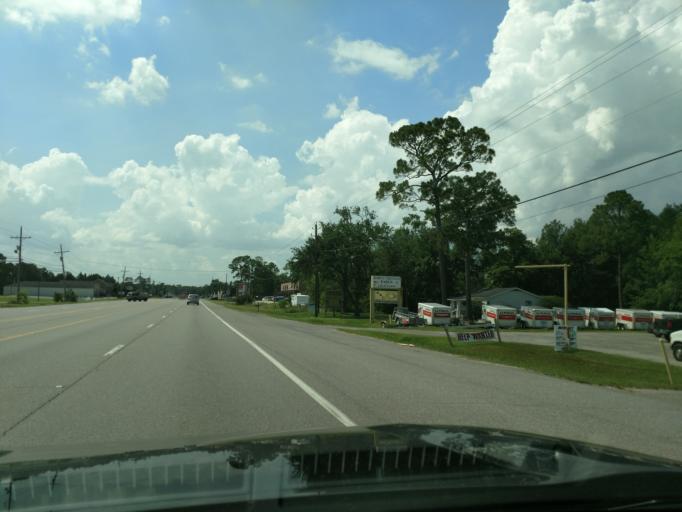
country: US
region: Mississippi
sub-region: Jackson County
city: Gulf Hills
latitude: 30.4364
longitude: -88.8312
